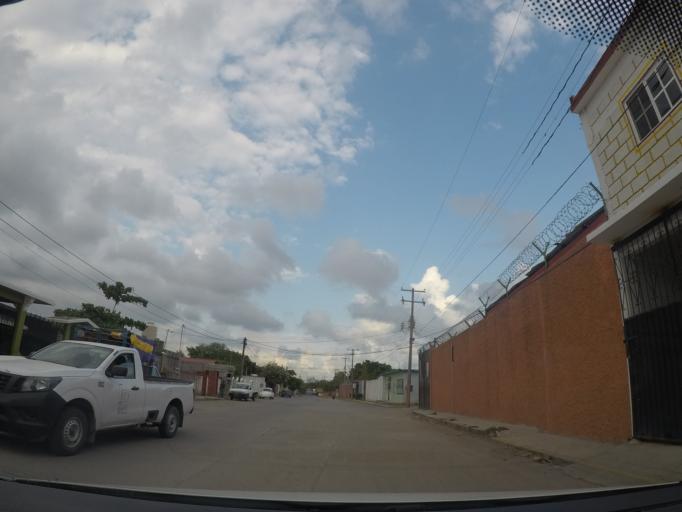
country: MX
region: Oaxaca
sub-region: Salina Cruz
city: Salina Cruz
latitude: 16.2130
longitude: -95.1956
